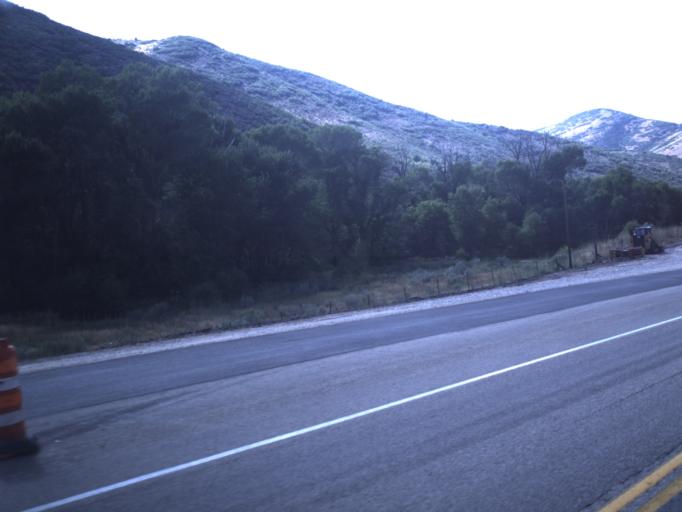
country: US
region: Utah
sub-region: Wasatch County
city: Heber
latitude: 40.4267
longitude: -111.3477
